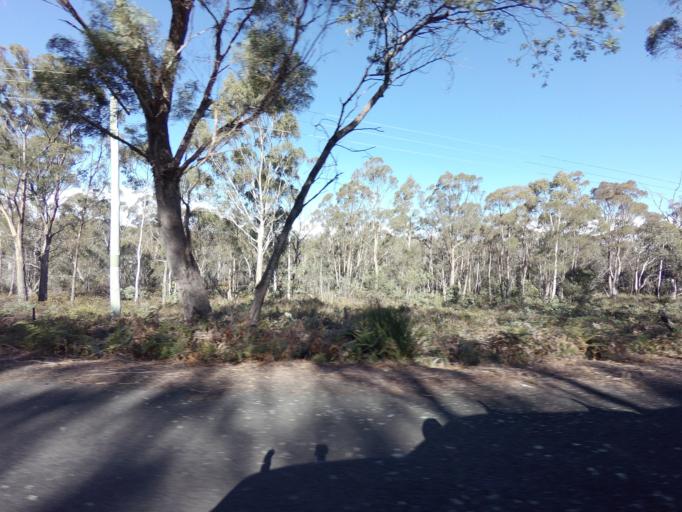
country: AU
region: Tasmania
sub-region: Sorell
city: Sorell
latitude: -42.3594
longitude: 147.9588
